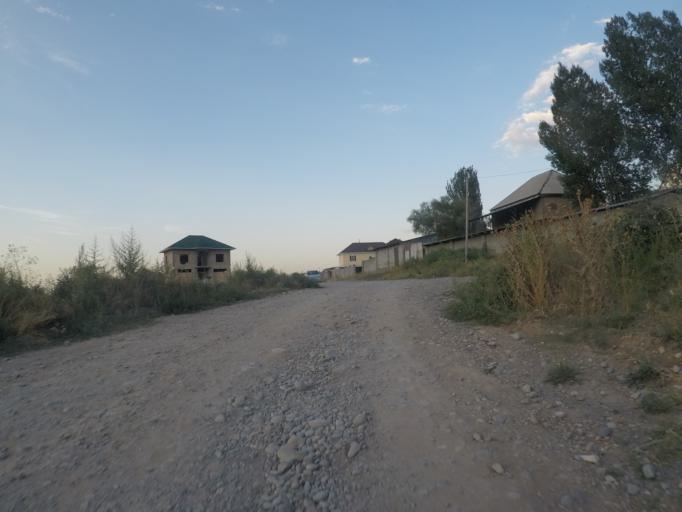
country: KG
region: Chuy
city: Bishkek
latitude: 42.7785
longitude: 74.6456
